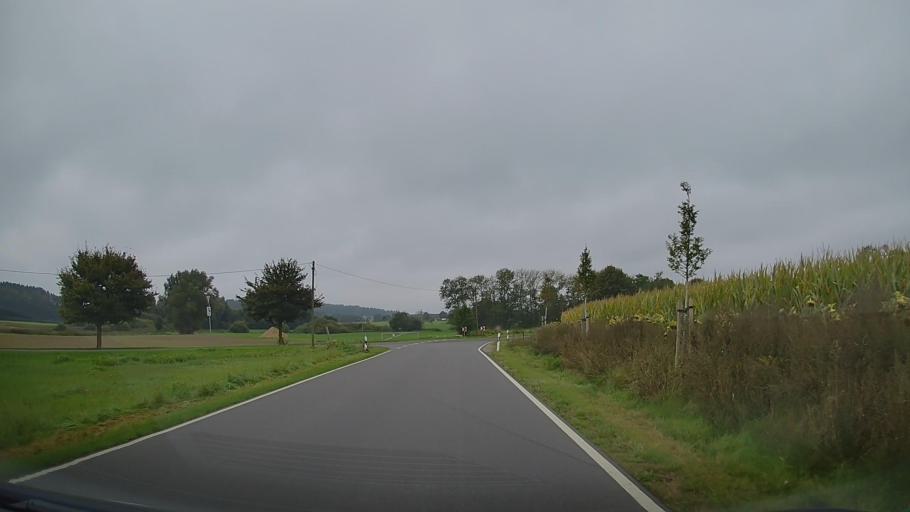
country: DE
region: Mecklenburg-Vorpommern
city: Dummerstorf
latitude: 53.9536
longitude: 12.2294
